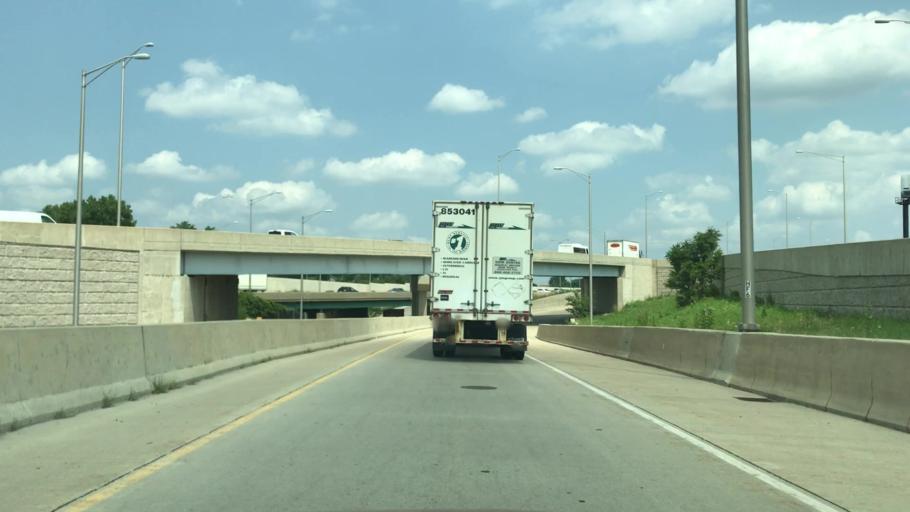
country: US
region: Illinois
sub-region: Will County
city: Bolingbrook
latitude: 41.6981
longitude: -88.0411
